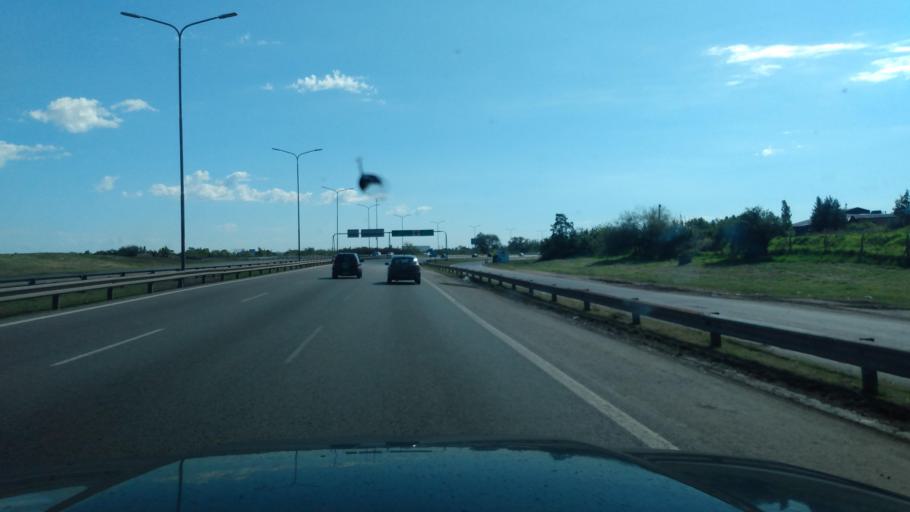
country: AR
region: Buenos Aires
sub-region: Partido de Tigre
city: Tigre
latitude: -34.4967
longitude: -58.5935
